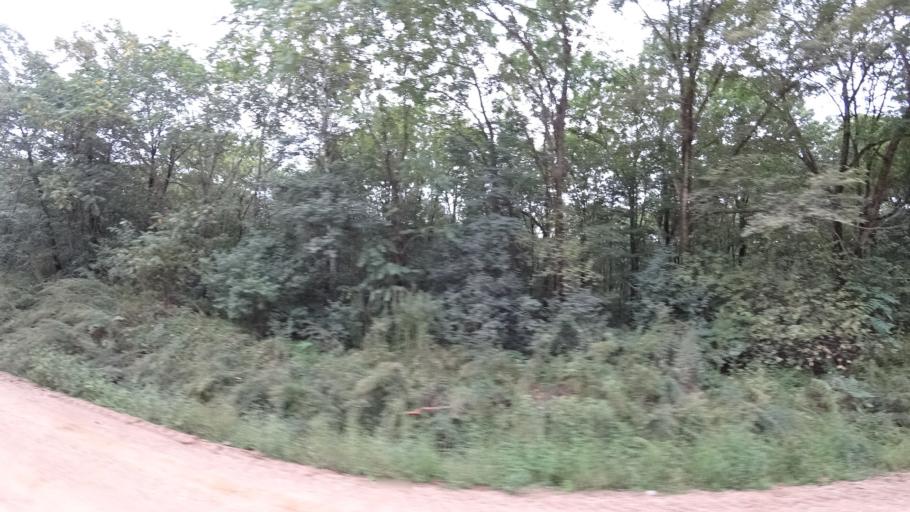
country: RU
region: Primorskiy
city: Rettikhovka
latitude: 44.2511
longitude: 132.6938
